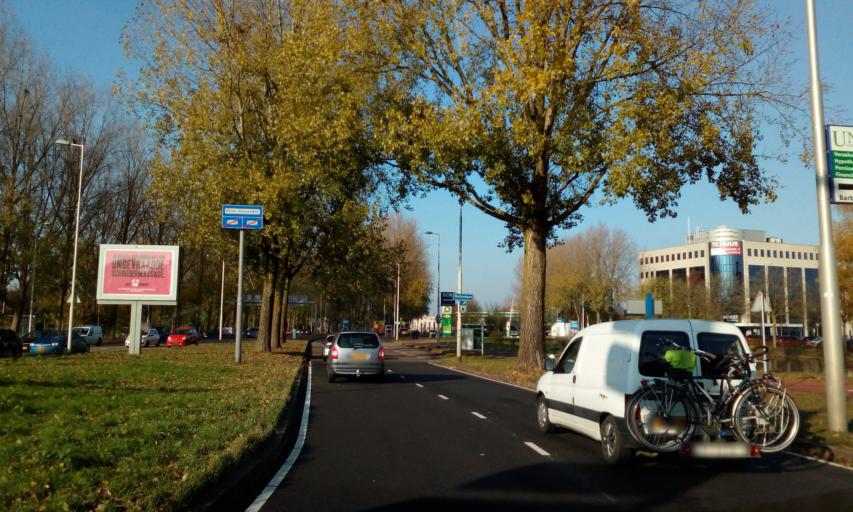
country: NL
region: South Holland
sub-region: Gemeente Capelle aan den IJssel
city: Capelle aan den IJssel
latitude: 51.9565
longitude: 4.5625
